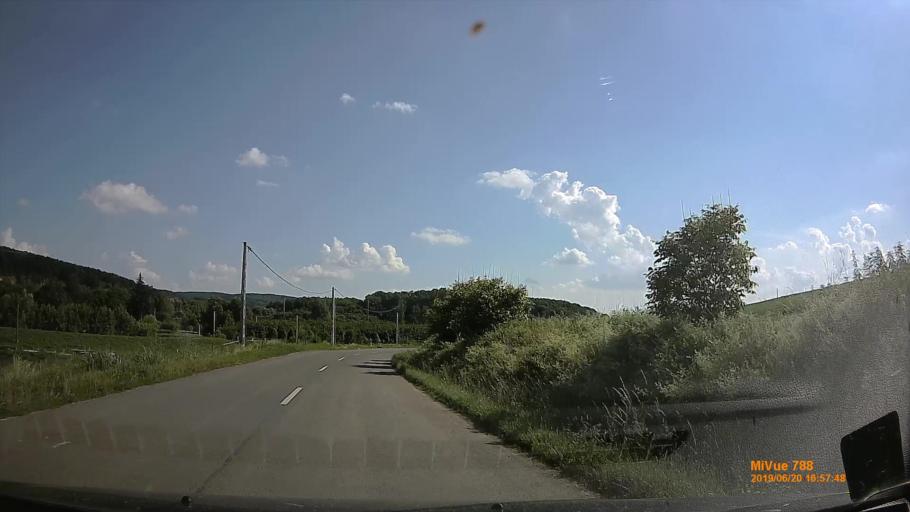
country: HU
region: Baranya
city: Buekkoesd
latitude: 46.1409
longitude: 18.0589
